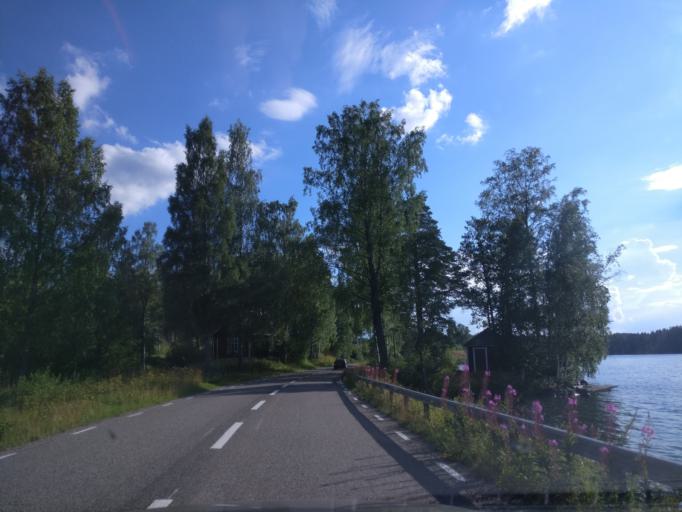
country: SE
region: Dalarna
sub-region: Ludvika Kommun
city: Ludvika
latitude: 60.3003
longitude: 15.2254
